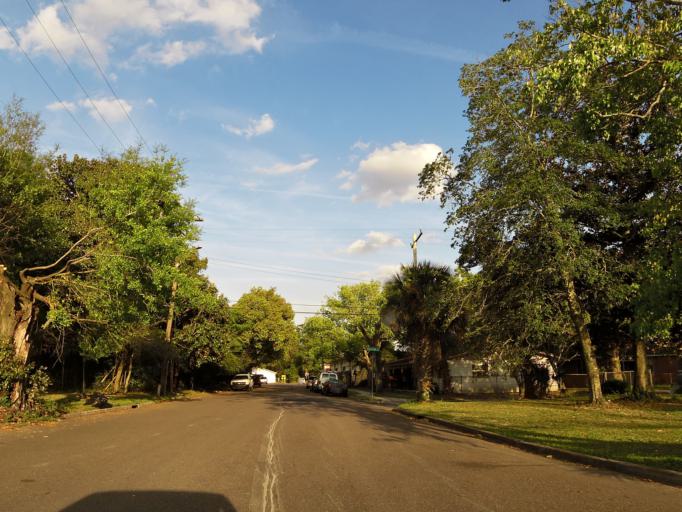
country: US
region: Florida
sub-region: Duval County
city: Jacksonville
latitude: 30.3477
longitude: -81.6859
